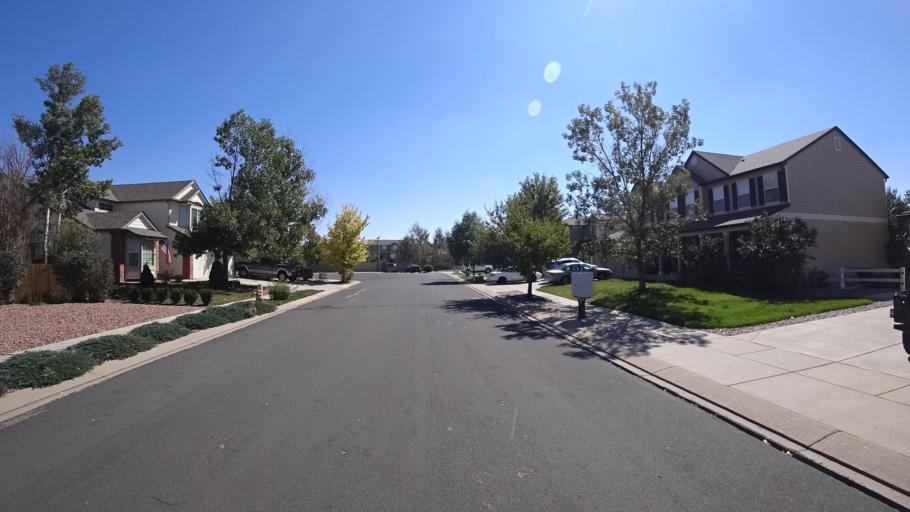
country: US
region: Colorado
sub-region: El Paso County
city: Cimarron Hills
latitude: 38.8951
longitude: -104.7030
